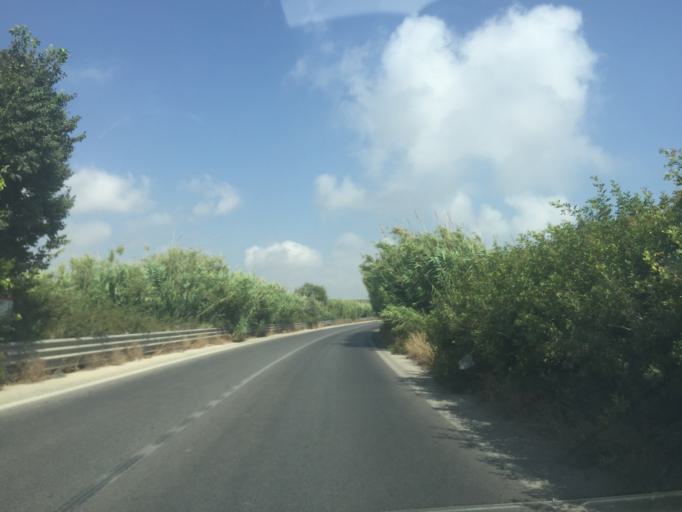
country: IT
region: Sicily
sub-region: Ragusa
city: Marina di Ragusa
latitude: 36.7785
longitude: 14.5941
